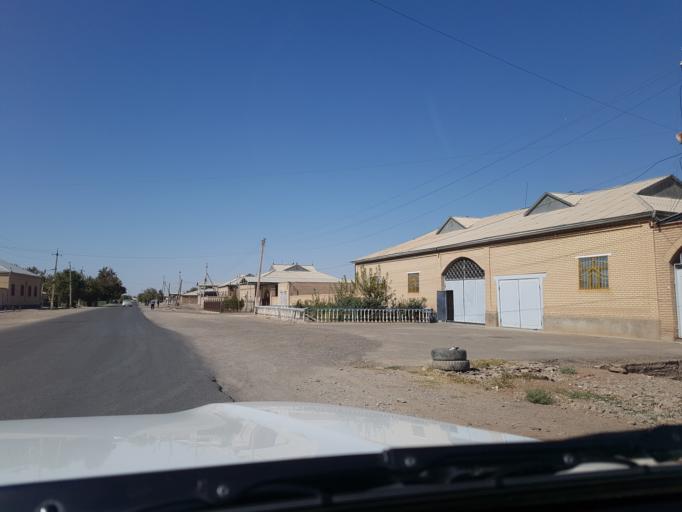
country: IR
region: Razavi Khorasan
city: Sarakhs
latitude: 36.5184
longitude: 61.2198
